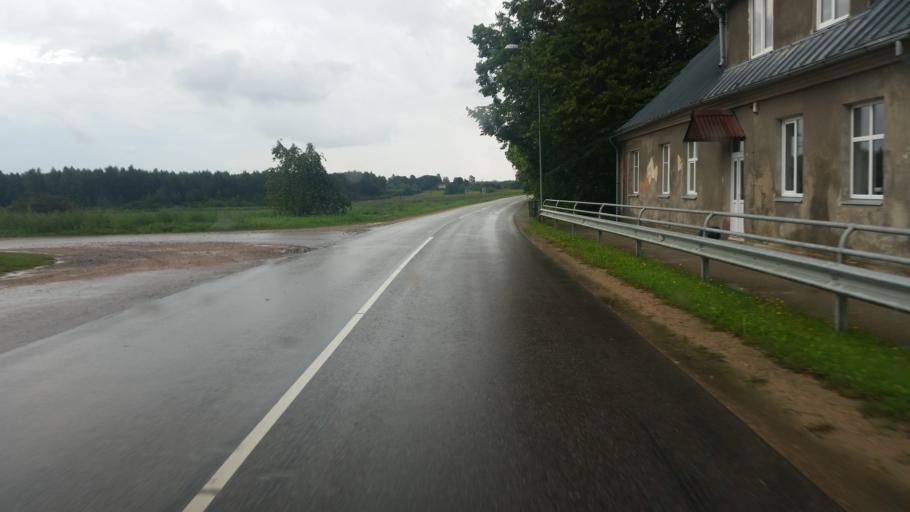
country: LV
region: Bauskas Rajons
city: Bauska
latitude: 56.4326
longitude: 24.3523
